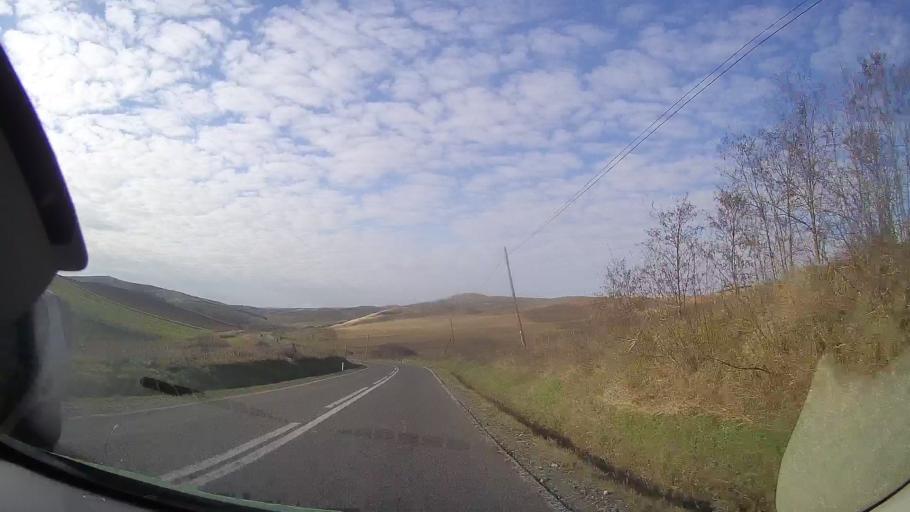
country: RO
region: Cluj
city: Jucu Herghelia
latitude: 46.8115
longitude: 23.8281
